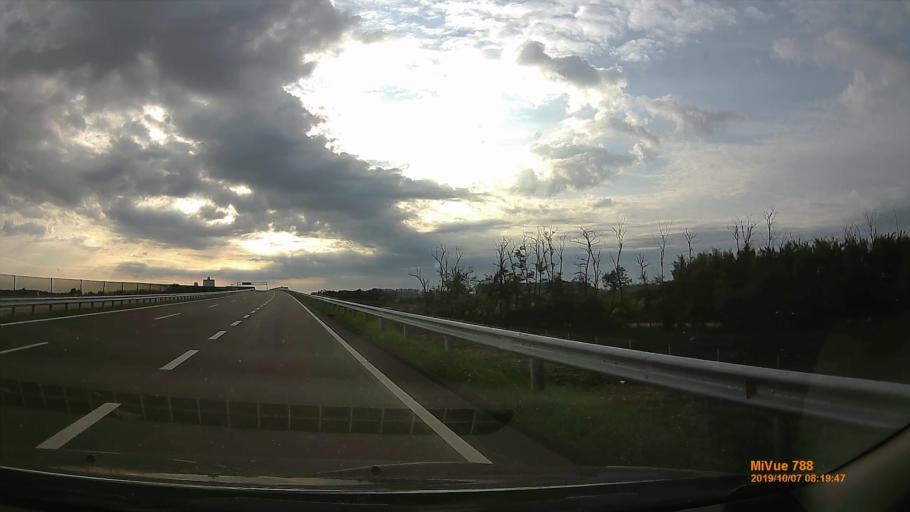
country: HU
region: Jasz-Nagykun-Szolnok
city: Kunszentmarton
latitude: 46.8702
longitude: 20.2687
